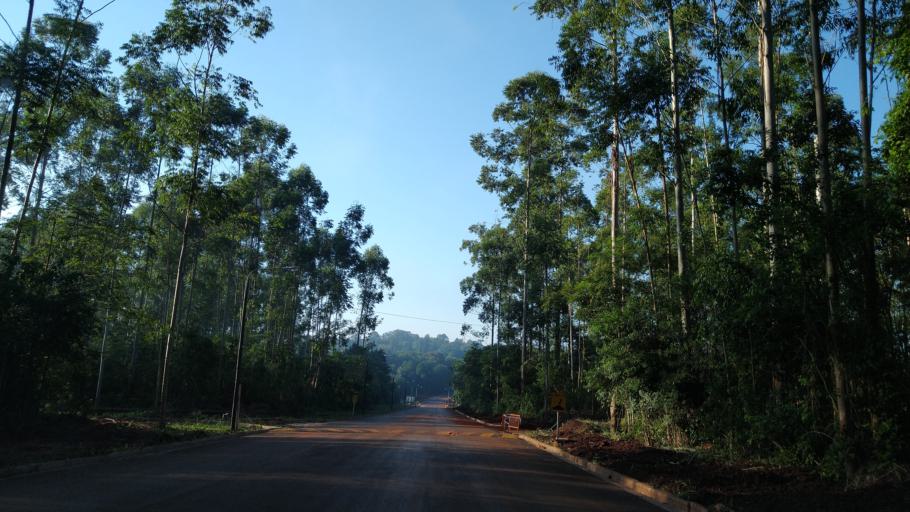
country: AR
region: Misiones
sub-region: Departamento de Montecarlo
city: Montecarlo
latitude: -26.5585
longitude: -54.7710
